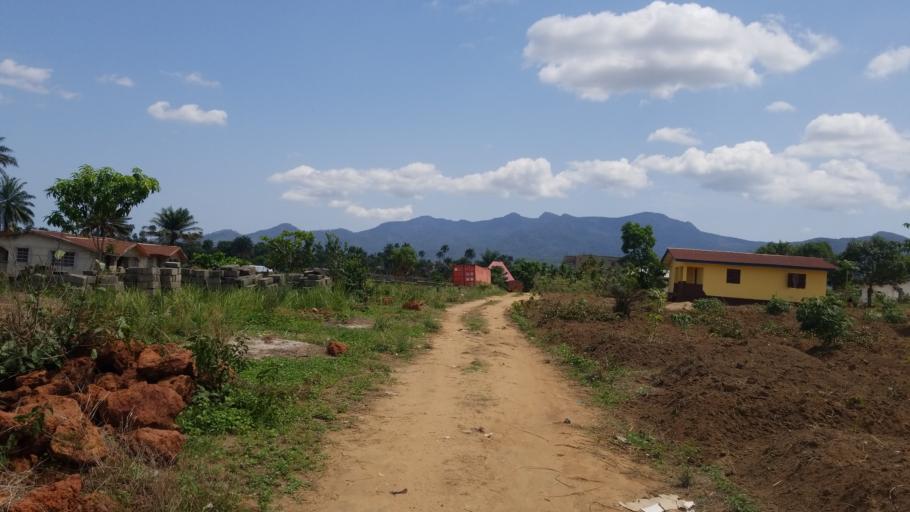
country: SL
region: Western Area
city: Waterloo
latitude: 8.3107
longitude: -13.0567
